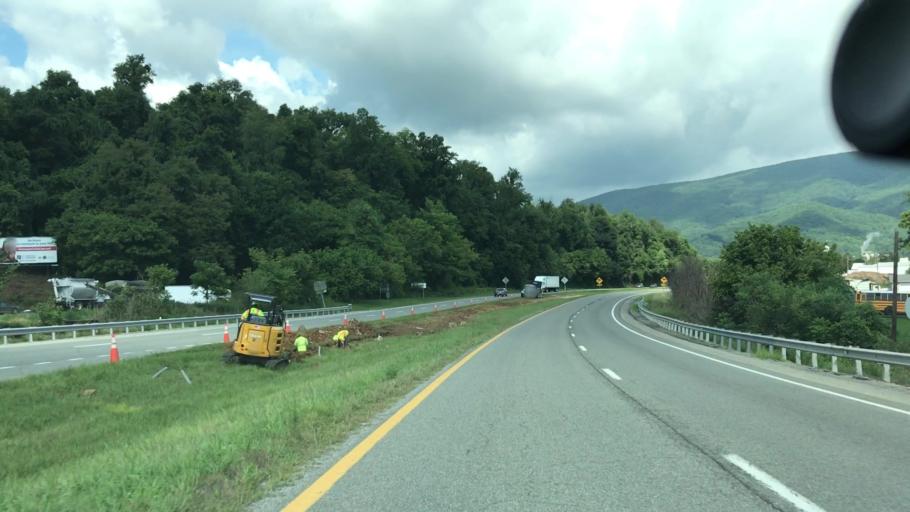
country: US
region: Virginia
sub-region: Giles County
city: Pearisburg
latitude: 37.3355
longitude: -80.7518
